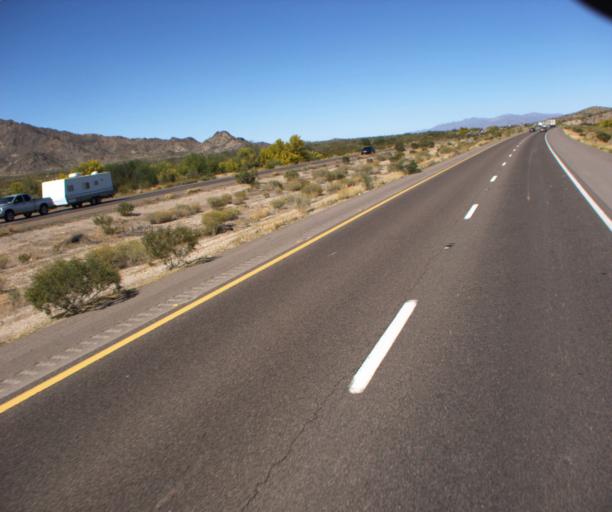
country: US
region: Arizona
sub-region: Maricopa County
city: Buckeye
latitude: 33.2416
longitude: -112.6393
